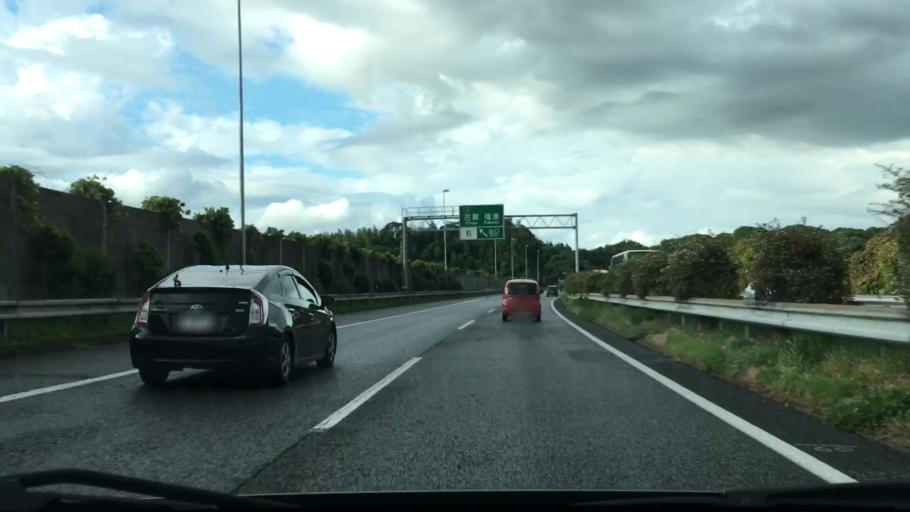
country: JP
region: Fukuoka
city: Koga
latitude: 33.7153
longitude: 130.4908
